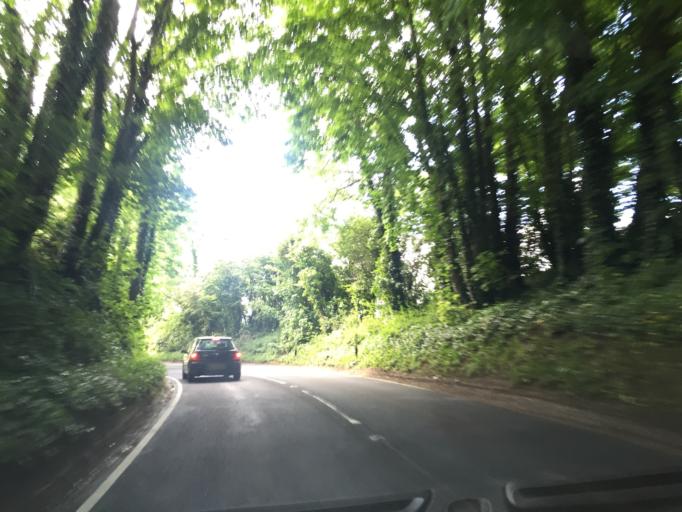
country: GB
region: England
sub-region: Dorset
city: Dorchester
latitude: 50.6970
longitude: -2.4036
